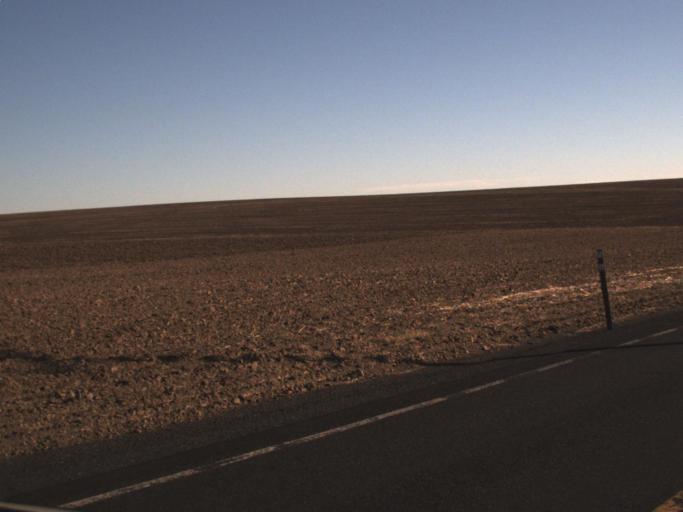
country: US
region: Washington
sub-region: Adams County
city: Ritzville
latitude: 47.0952
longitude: -118.3654
